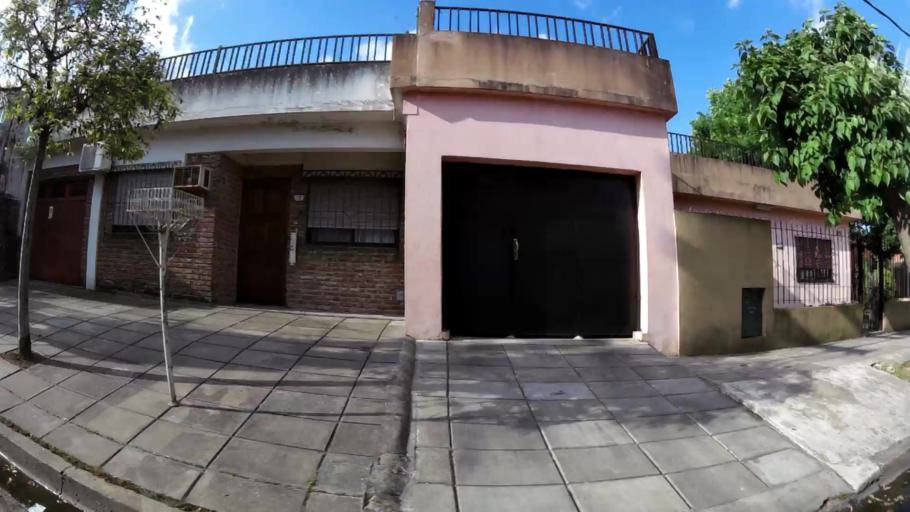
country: AR
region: Buenos Aires
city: San Justo
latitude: -34.6967
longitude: -58.5879
